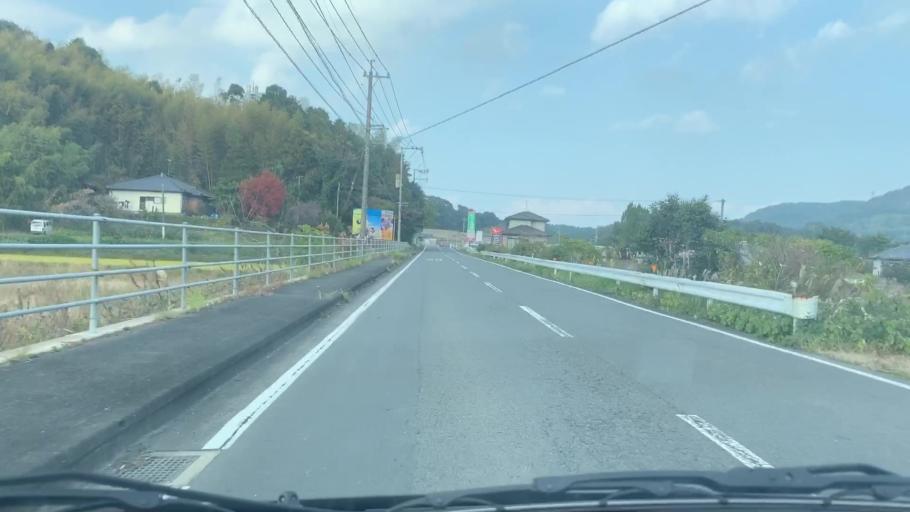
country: JP
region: Nagasaki
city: Togitsu
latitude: 32.9659
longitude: 129.7807
